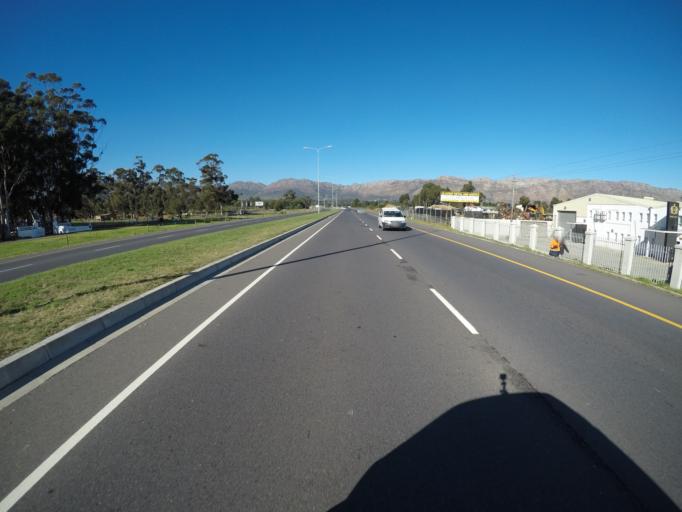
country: ZA
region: Western Cape
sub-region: Overberg District Municipality
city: Grabouw
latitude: -34.1207
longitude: 18.8815
